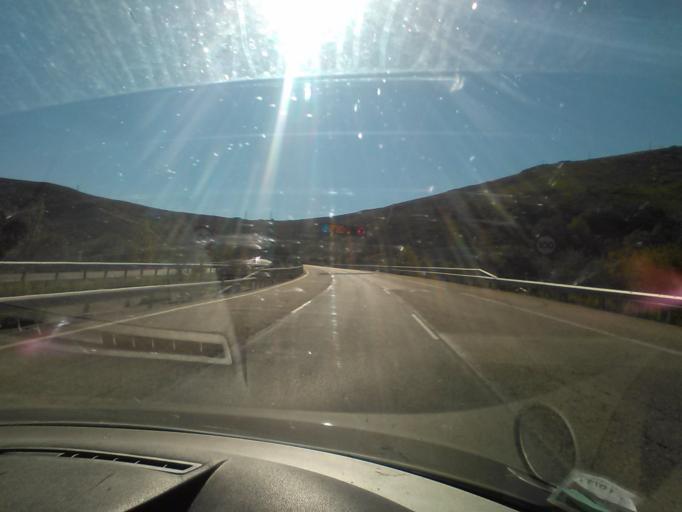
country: ES
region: Castille and Leon
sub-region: Provincia de Zamora
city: Lubian
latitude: 42.0395
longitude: -6.9575
